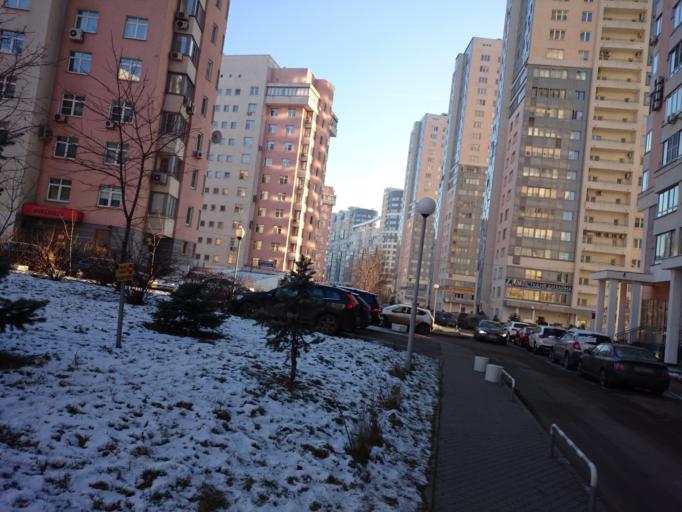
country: RU
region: Moscow
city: Sokol
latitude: 55.7888
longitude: 37.5196
